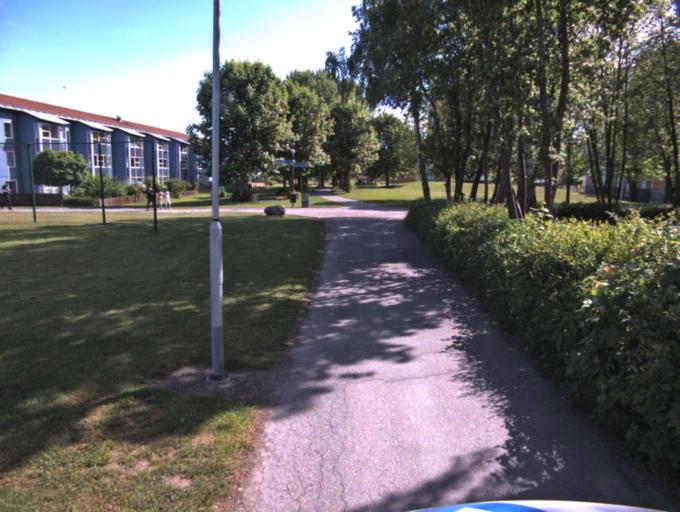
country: SE
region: Skane
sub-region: Kristianstads Kommun
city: Kristianstad
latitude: 56.0421
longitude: 14.1833
